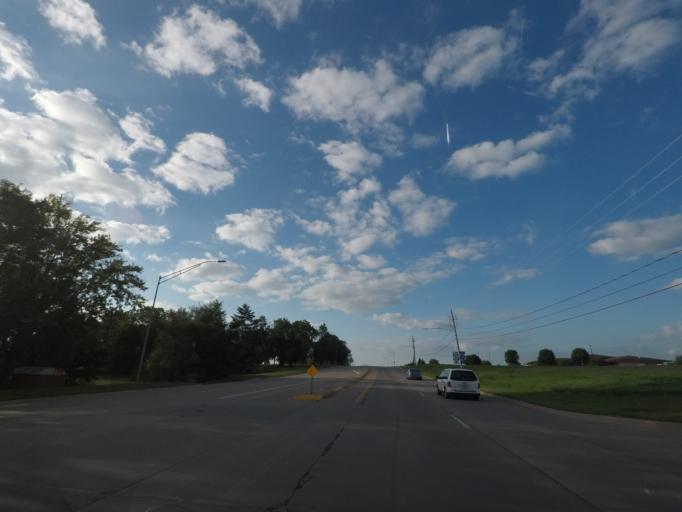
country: US
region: Iowa
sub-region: Warren County
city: Norwalk
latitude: 41.5183
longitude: -93.6450
